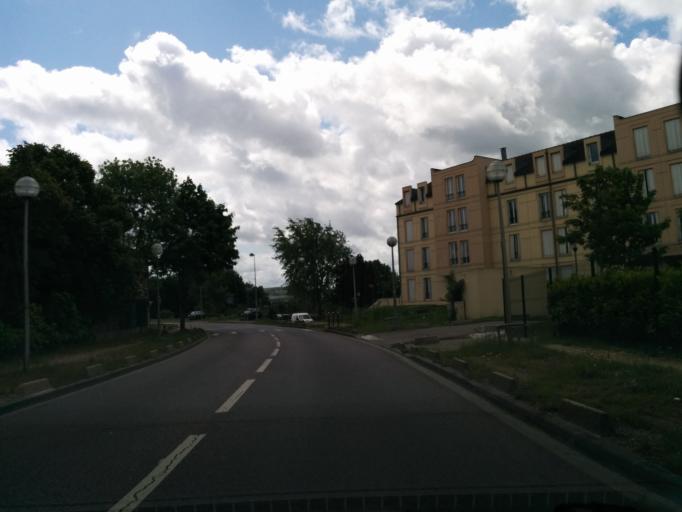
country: FR
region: Ile-de-France
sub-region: Departement des Yvelines
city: Limay
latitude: 48.9921
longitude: 1.7275
